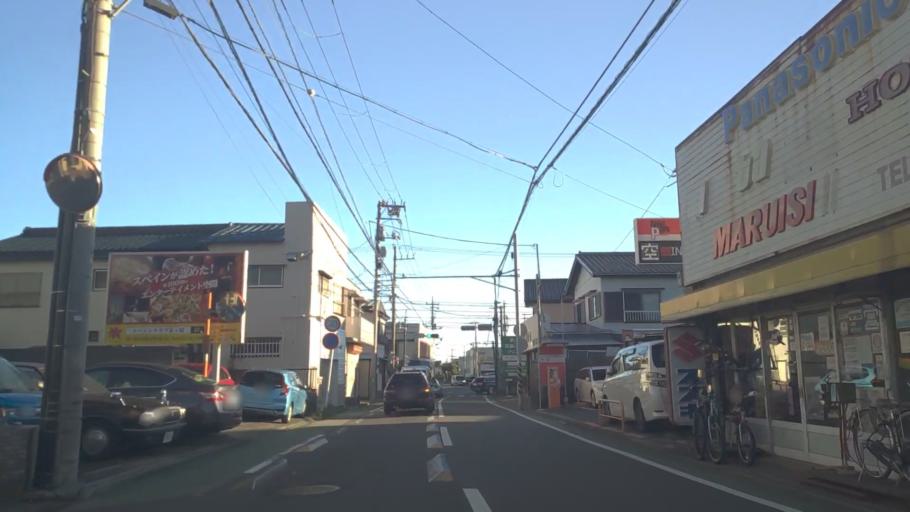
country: JP
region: Kanagawa
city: Chigasaki
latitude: 35.3256
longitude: 139.4149
